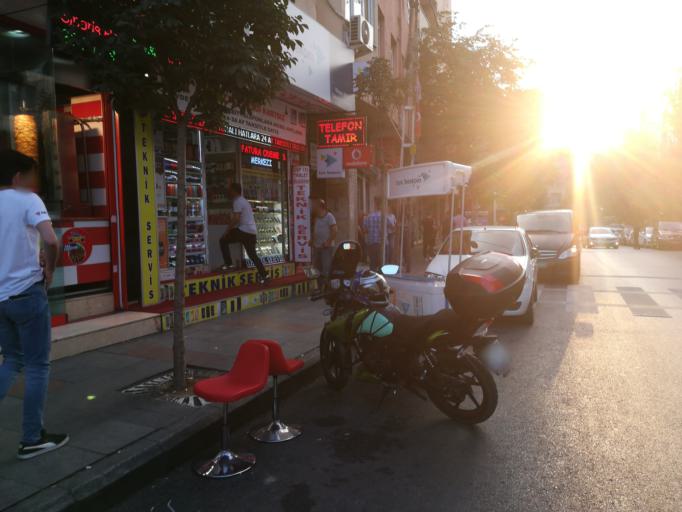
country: TR
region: Istanbul
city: Sisli
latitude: 41.0995
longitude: 28.9933
